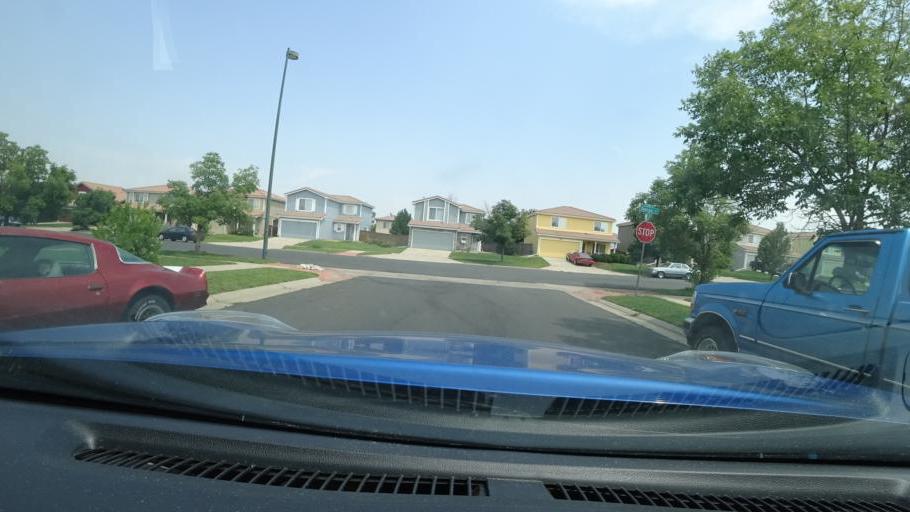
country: US
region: Colorado
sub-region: Adams County
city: Aurora
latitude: 39.7729
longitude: -104.7394
